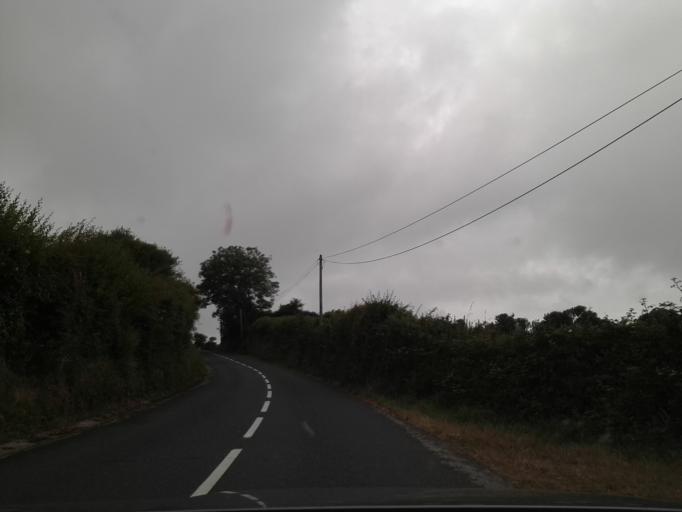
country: FR
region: Lower Normandy
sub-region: Departement de la Manche
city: Beaumont-Hague
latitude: 49.6822
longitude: -1.8544
